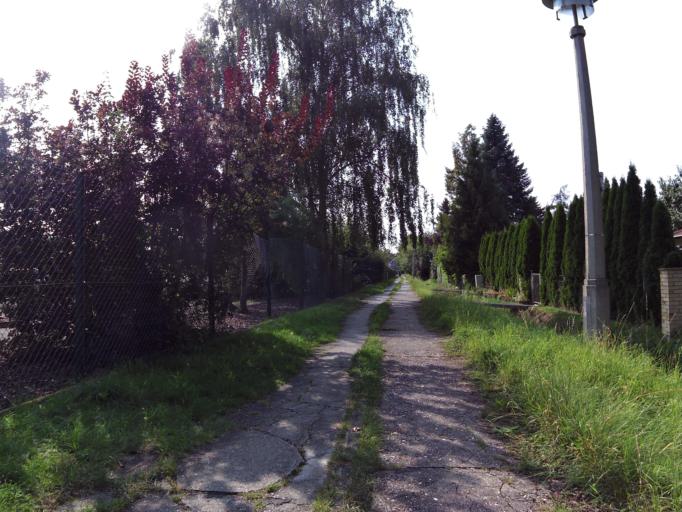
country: DE
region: Saxony
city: Rackwitz
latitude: 51.3886
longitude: 12.3861
